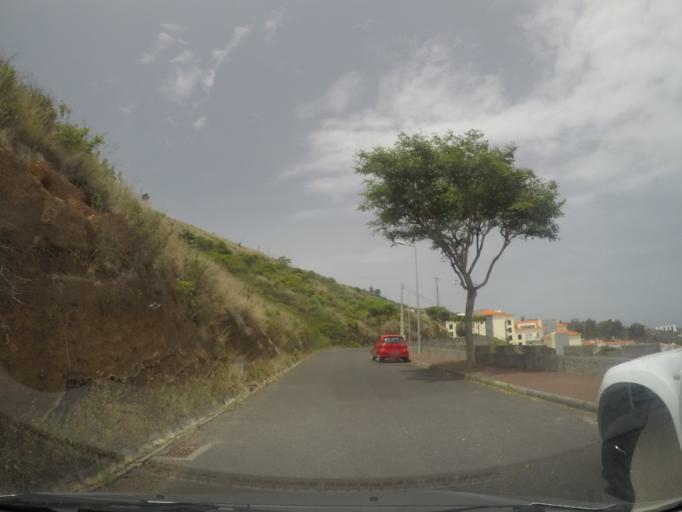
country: PT
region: Madeira
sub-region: Santa Cruz
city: Camacha
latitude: 32.6581
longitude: -16.8312
